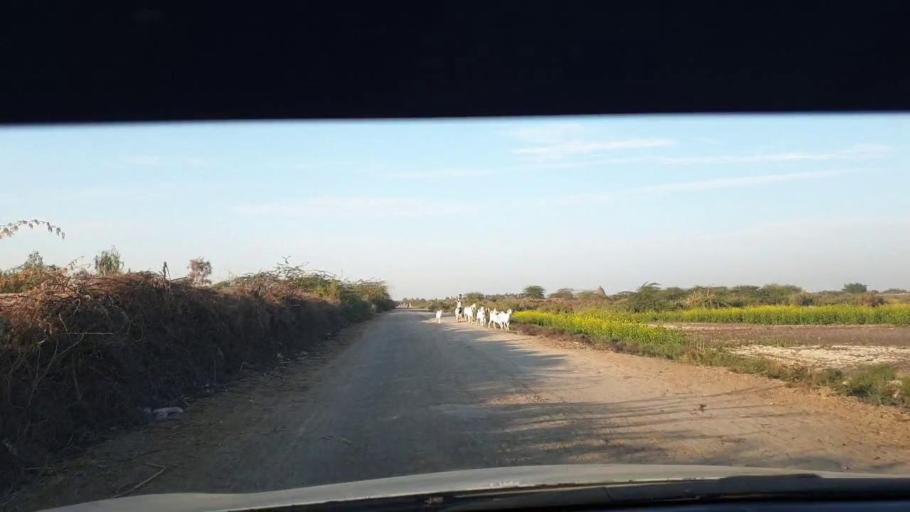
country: PK
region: Sindh
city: Berani
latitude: 25.8060
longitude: 68.8823
